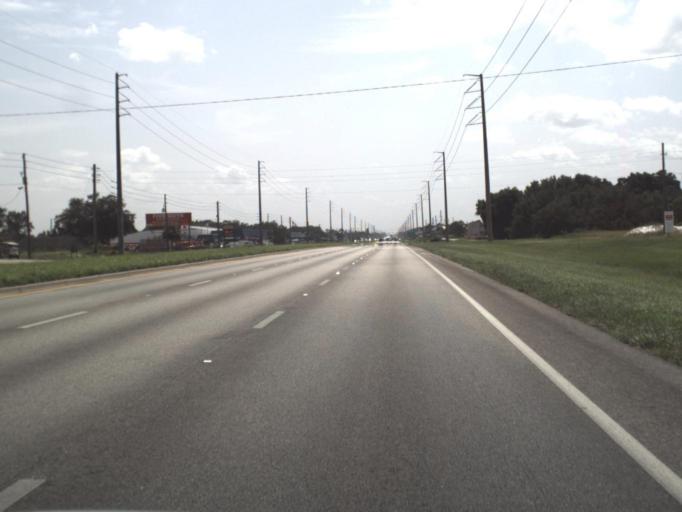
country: US
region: Florida
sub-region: Highlands County
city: Avon Park
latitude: 27.5472
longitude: -81.5070
